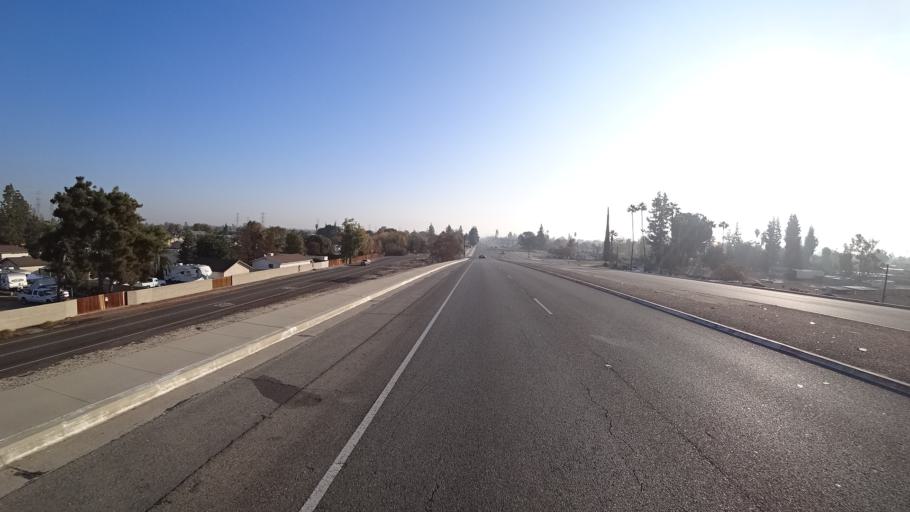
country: US
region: California
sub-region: Kern County
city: Greenacres
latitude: 35.3836
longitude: -119.1265
